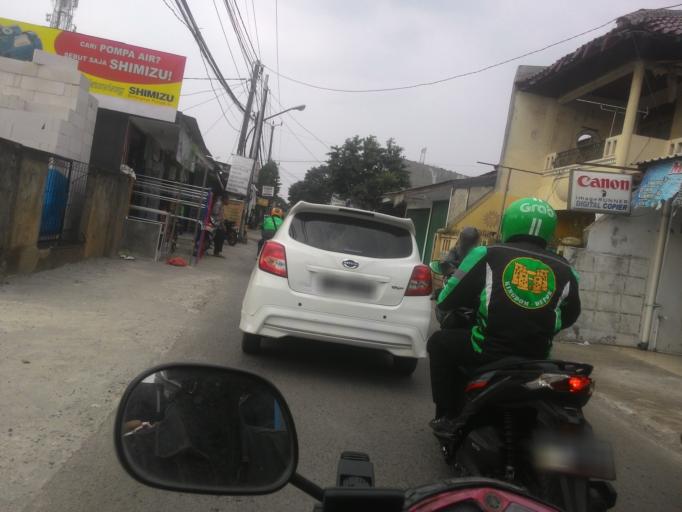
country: ID
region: West Java
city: Depok
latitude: -6.4252
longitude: 106.8373
